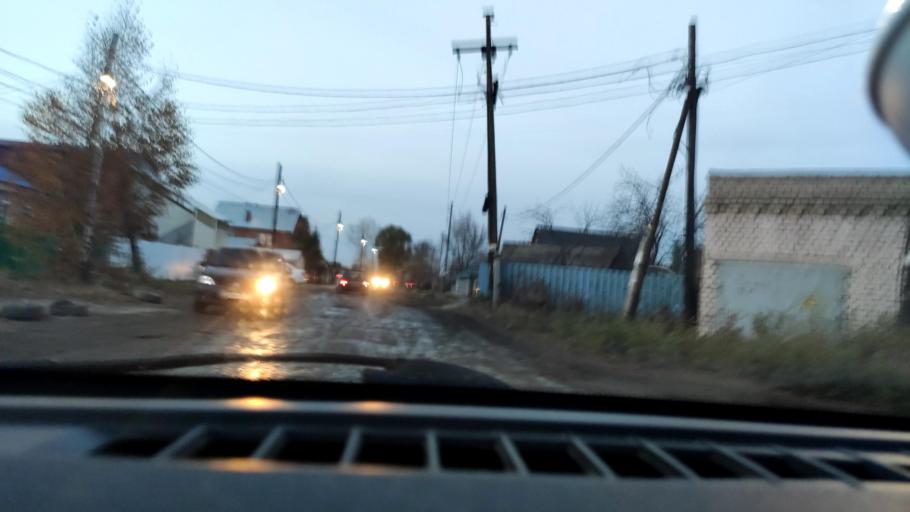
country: RU
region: Samara
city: Samara
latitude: 53.1331
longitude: 50.0949
